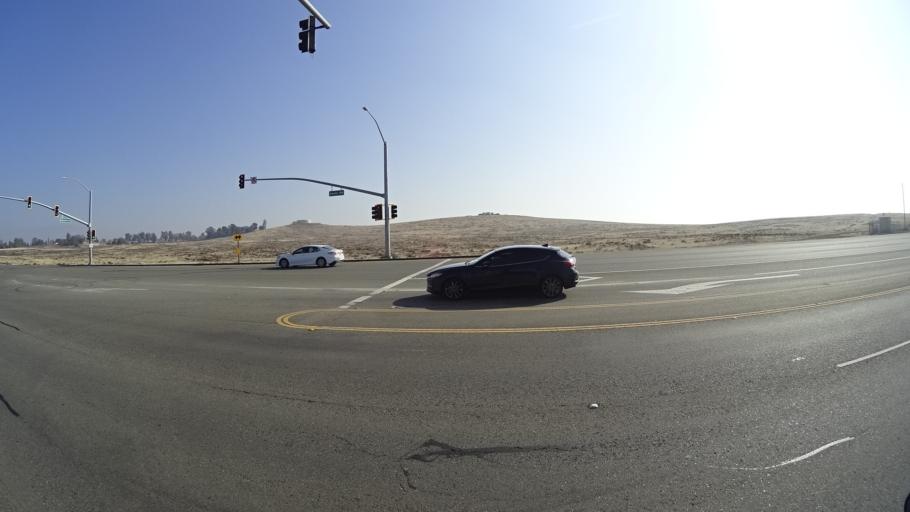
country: US
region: California
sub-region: Kern County
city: Oildale
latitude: 35.4000
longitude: -118.8775
